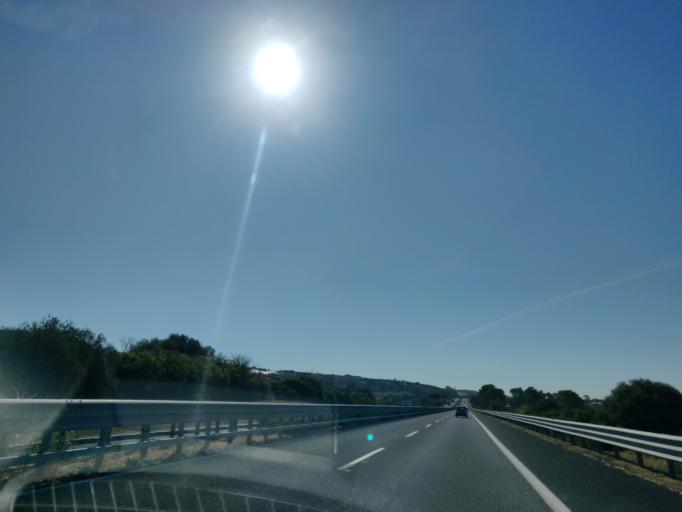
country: IT
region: Latium
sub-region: Citta metropolitana di Roma Capitale
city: Santa Marinella
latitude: 42.0498
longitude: 11.8320
